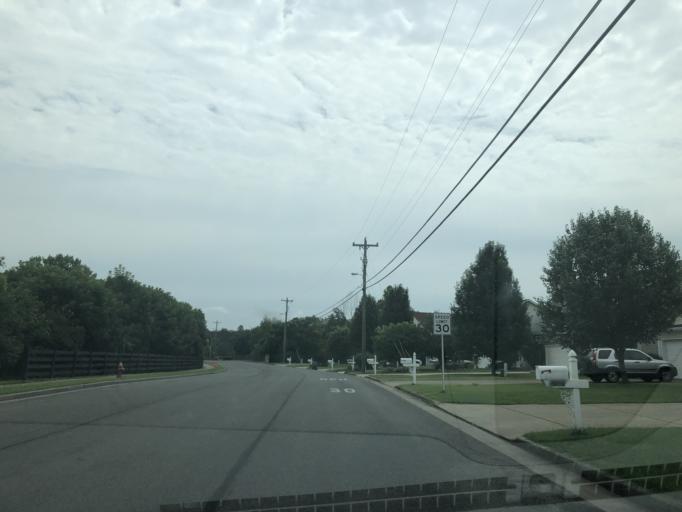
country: US
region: Tennessee
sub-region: Williamson County
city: Nolensville
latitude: 36.0199
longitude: -86.6803
